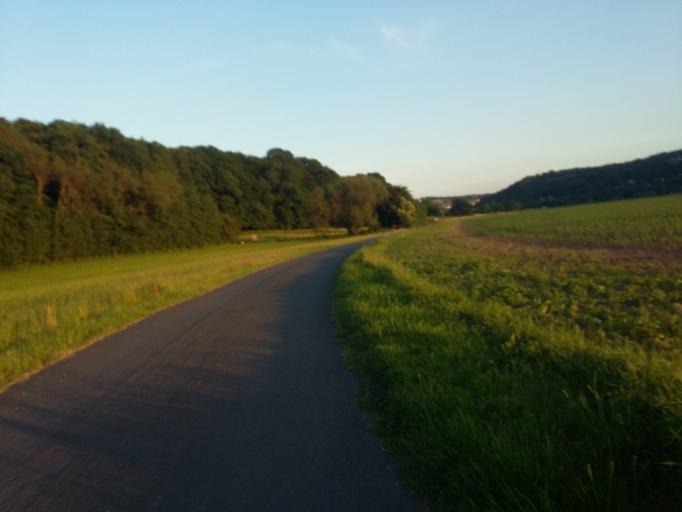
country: DE
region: North Rhine-Westphalia
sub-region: Regierungsbezirk Detmold
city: Vlotho
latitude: 52.1921
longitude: 8.8655
